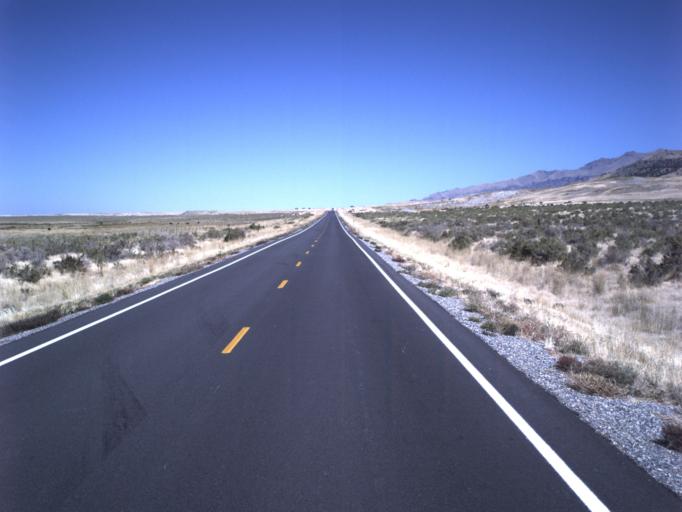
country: US
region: Utah
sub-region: Tooele County
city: Grantsville
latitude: 40.5507
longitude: -112.7404
